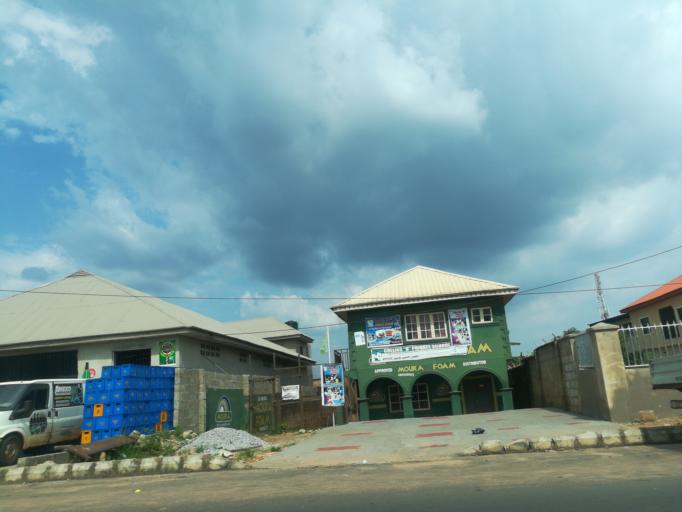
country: NG
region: Oyo
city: Ibadan
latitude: 7.4266
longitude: 3.8411
